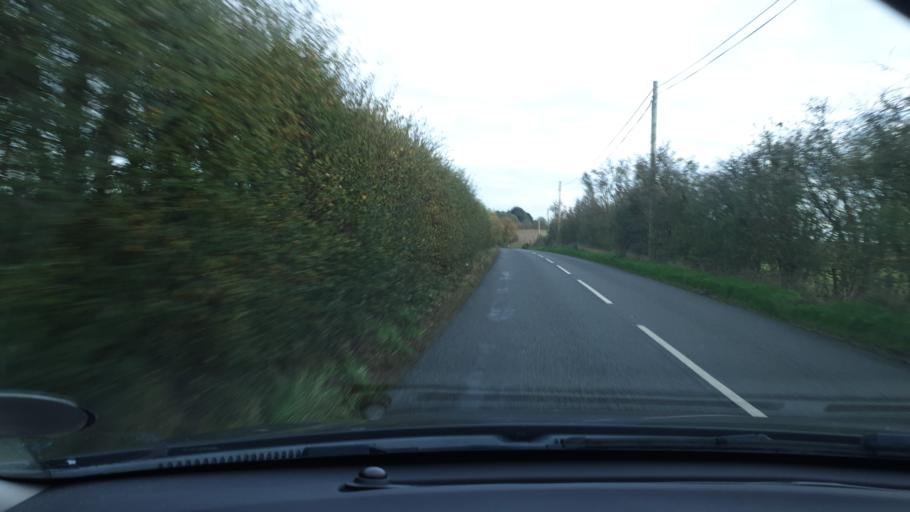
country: GB
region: England
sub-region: Essex
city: Mistley
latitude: 51.9262
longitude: 1.1198
